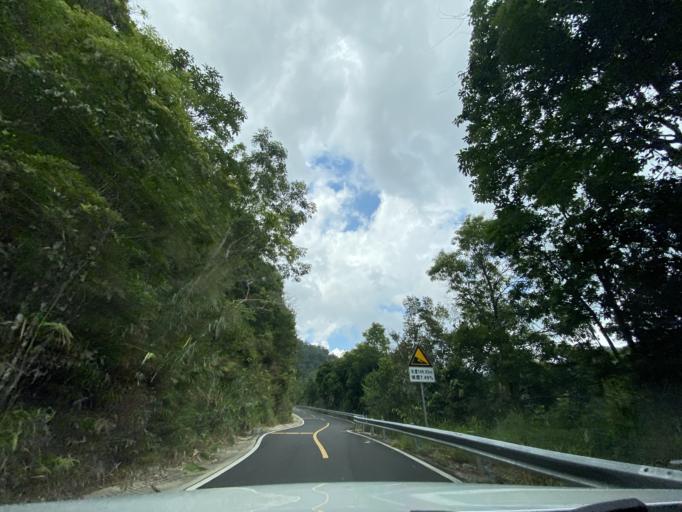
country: CN
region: Hainan
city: Benhao
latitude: 18.6787
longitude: 109.8800
